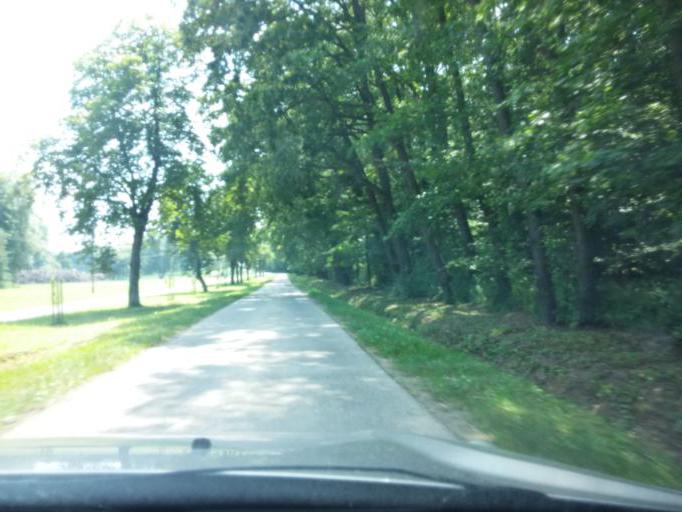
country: HU
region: Somogy
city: Kaposvar
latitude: 46.2467
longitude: 17.7761
